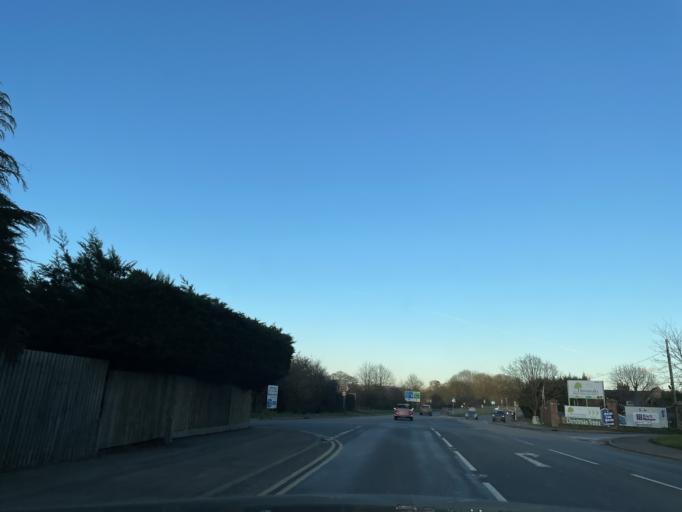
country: GB
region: England
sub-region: Kent
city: Halstead
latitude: 51.2810
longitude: 0.1420
